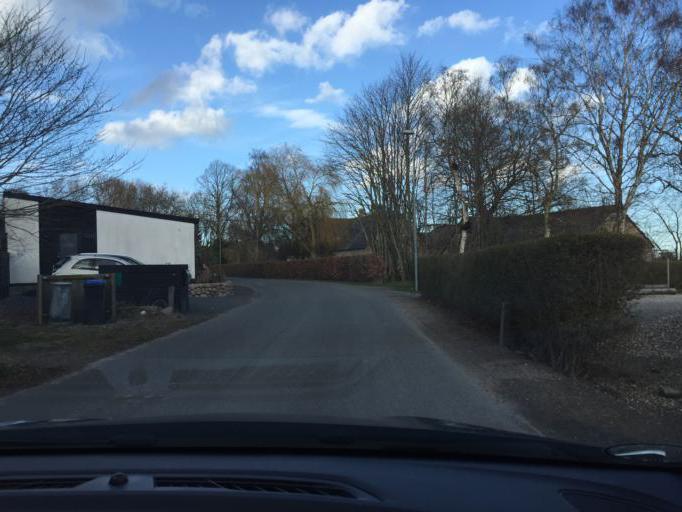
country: DK
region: South Denmark
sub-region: Nyborg Kommune
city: Ullerslev
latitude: 55.3522
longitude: 10.7215
